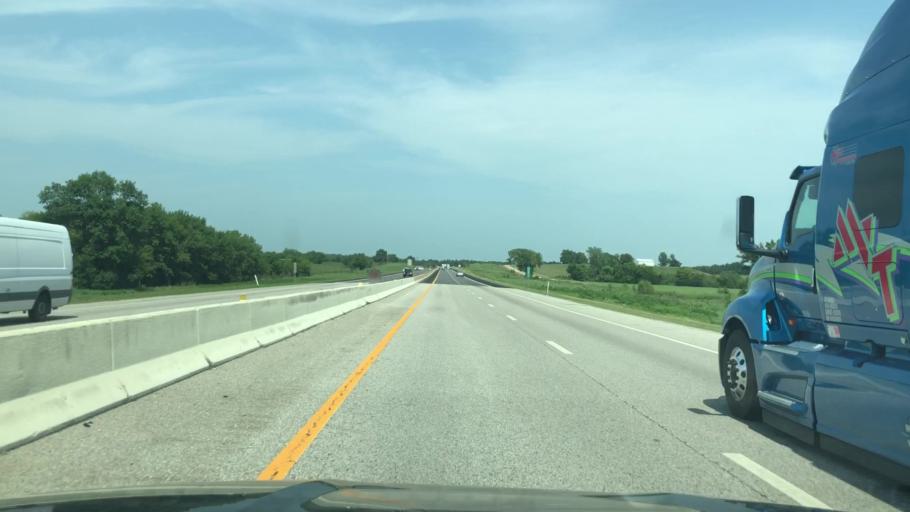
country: US
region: Oklahoma
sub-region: Craig County
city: Vinita
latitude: 36.6485
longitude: -95.1118
